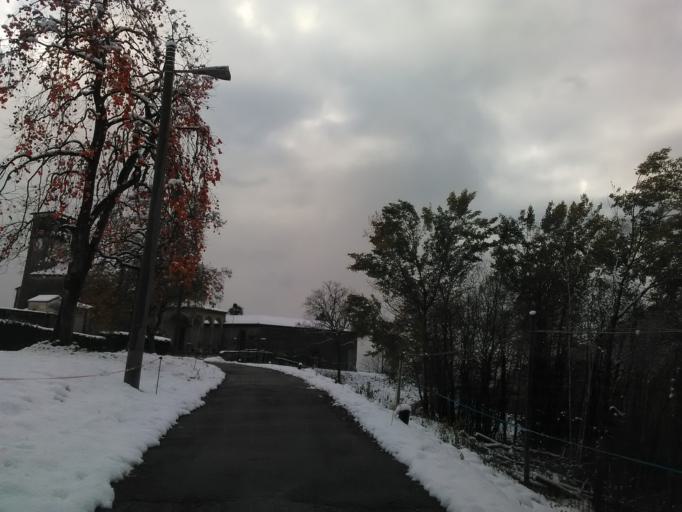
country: IT
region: Piedmont
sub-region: Provincia di Vercelli
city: Varallo
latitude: 45.7883
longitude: 8.2579
